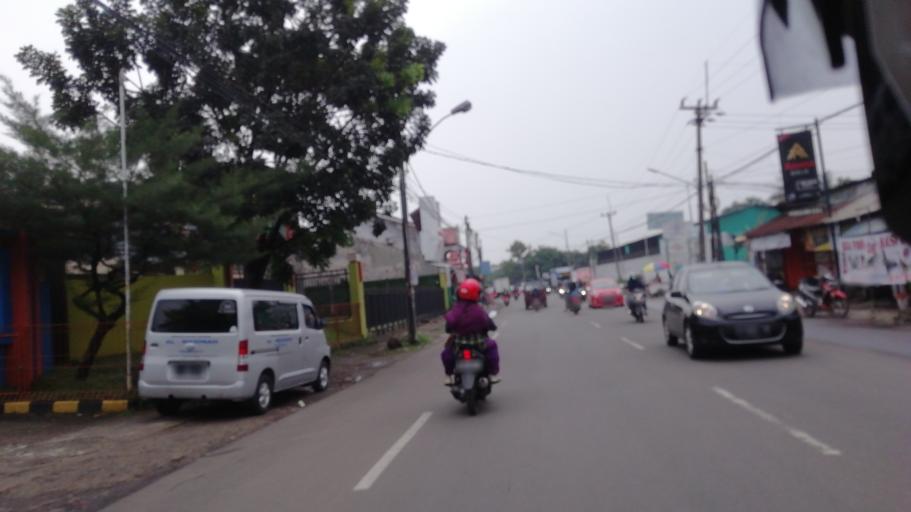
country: ID
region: West Java
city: Cibinong
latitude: -6.5170
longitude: 106.8081
